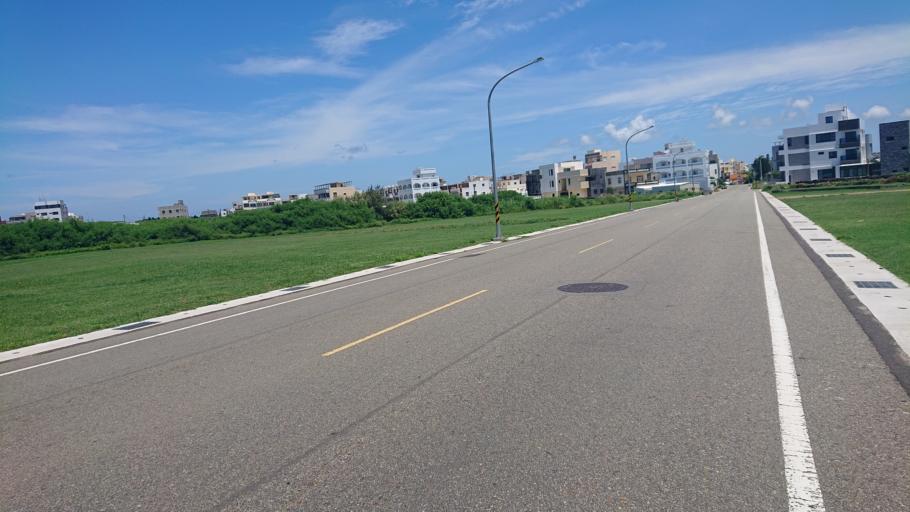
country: TW
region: Taiwan
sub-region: Penghu
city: Ma-kung
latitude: 23.5763
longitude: 119.5805
